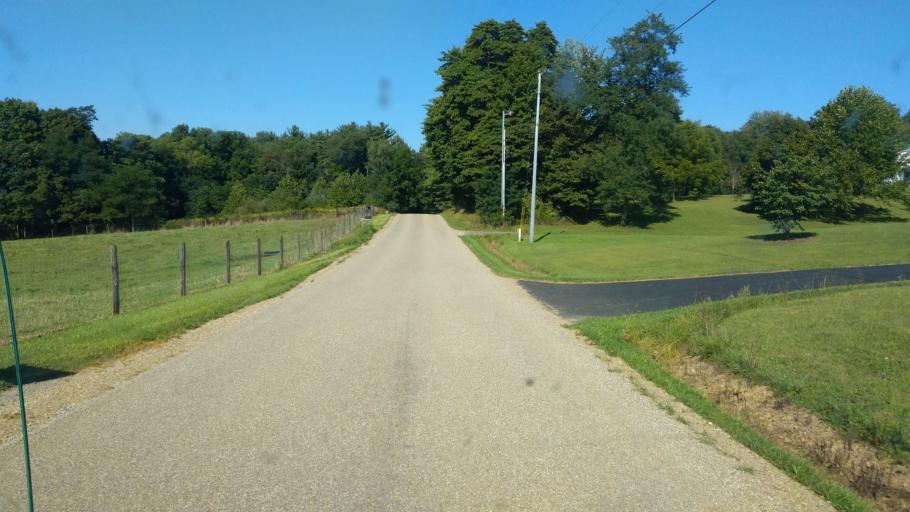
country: US
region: Ohio
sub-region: Knox County
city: Gambier
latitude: 40.4326
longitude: -82.3691
